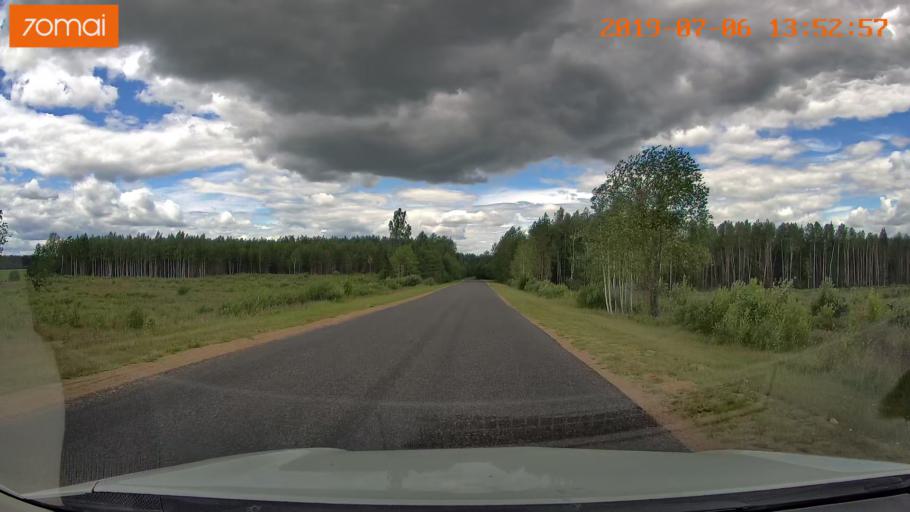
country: BY
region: Minsk
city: Ivyanyets
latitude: 53.7275
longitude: 26.8268
